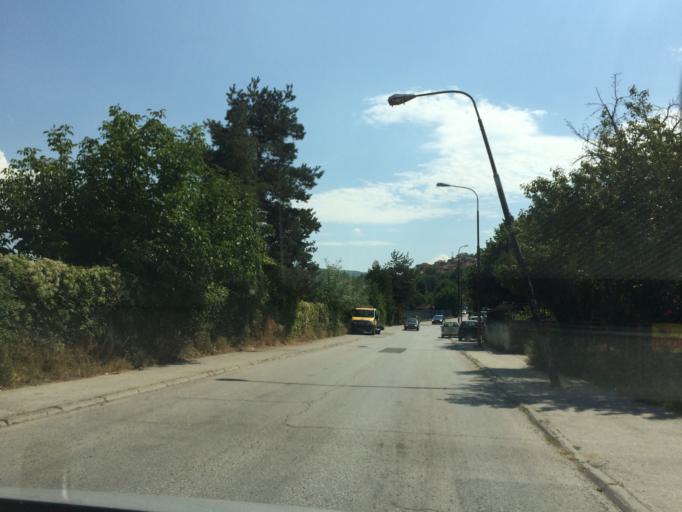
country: RS
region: Central Serbia
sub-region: Zlatiborski Okrug
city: Prijepolje
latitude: 43.3682
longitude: 19.6284
